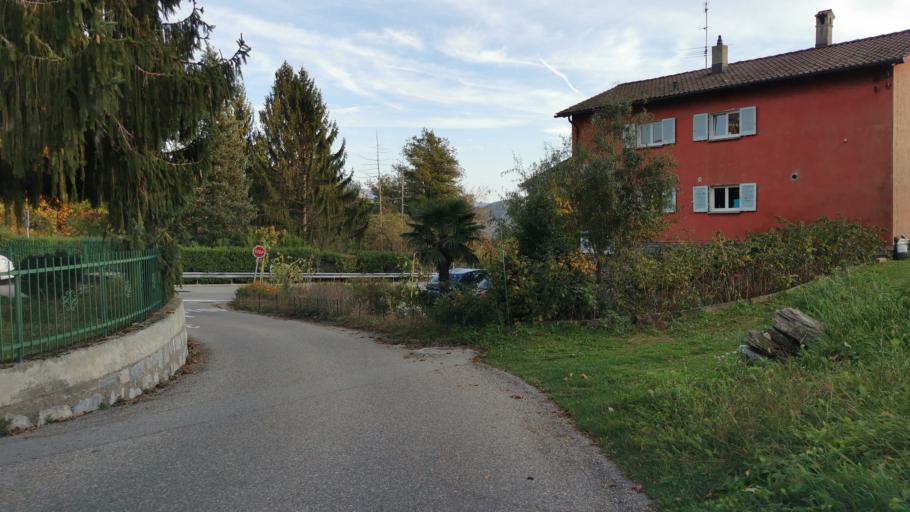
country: CH
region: Ticino
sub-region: Lugano District
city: Pura
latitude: 46.0233
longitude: 8.8562
